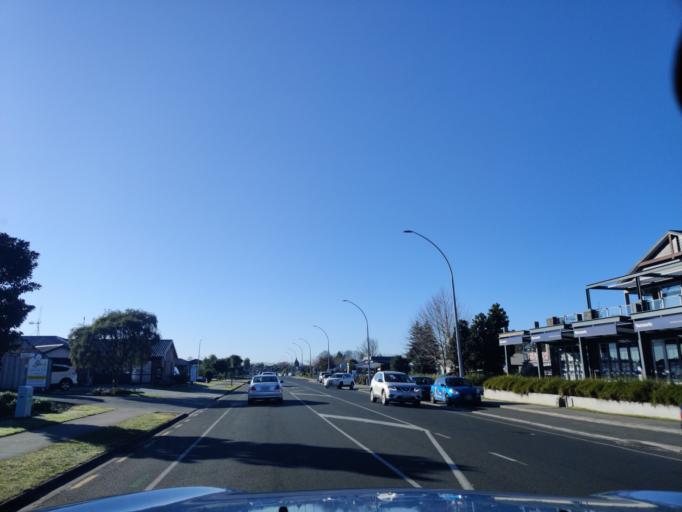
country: NZ
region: Waikato
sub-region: Hamilton City
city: Hamilton
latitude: -37.7306
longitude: 175.2744
